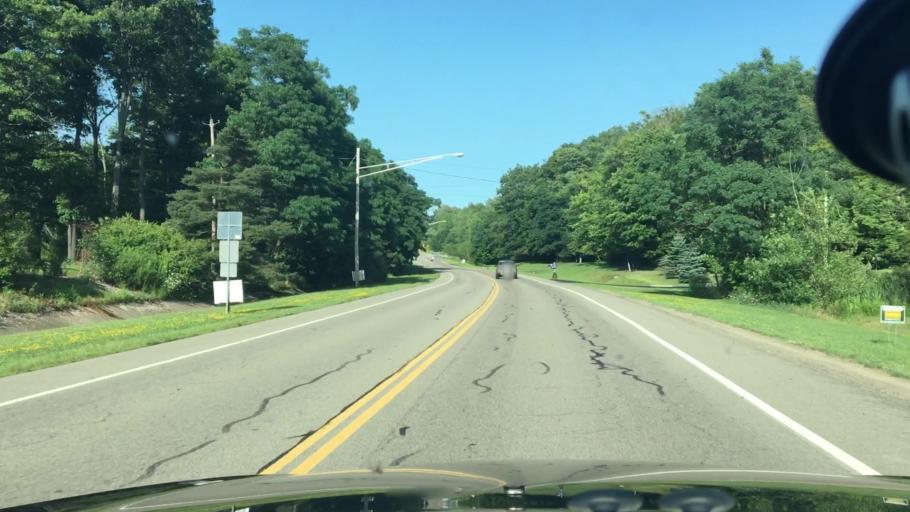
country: US
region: New York
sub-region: Erie County
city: Angola
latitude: 42.6503
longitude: -79.0319
